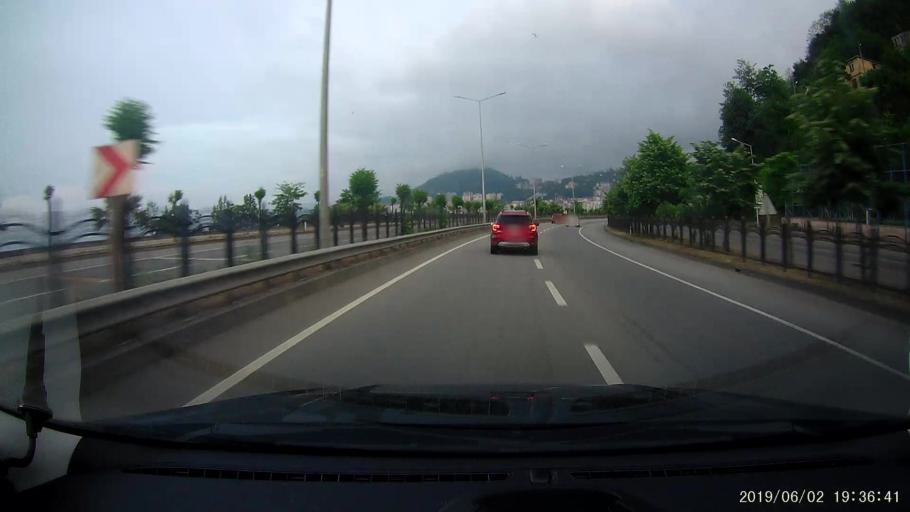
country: TR
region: Giresun
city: Giresun
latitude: 40.9246
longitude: 38.3910
